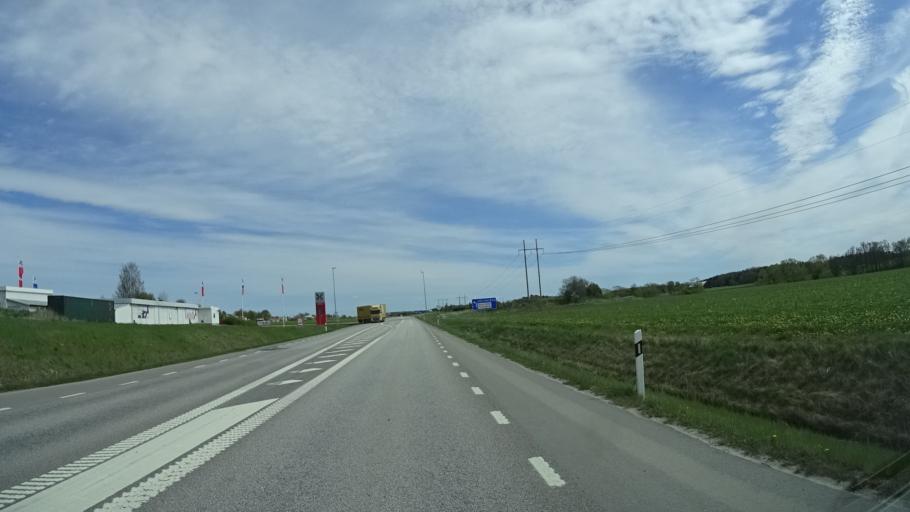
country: SE
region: OEstergoetland
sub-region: Linkopings Kommun
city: Vikingstad
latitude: 58.3763
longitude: 15.4252
